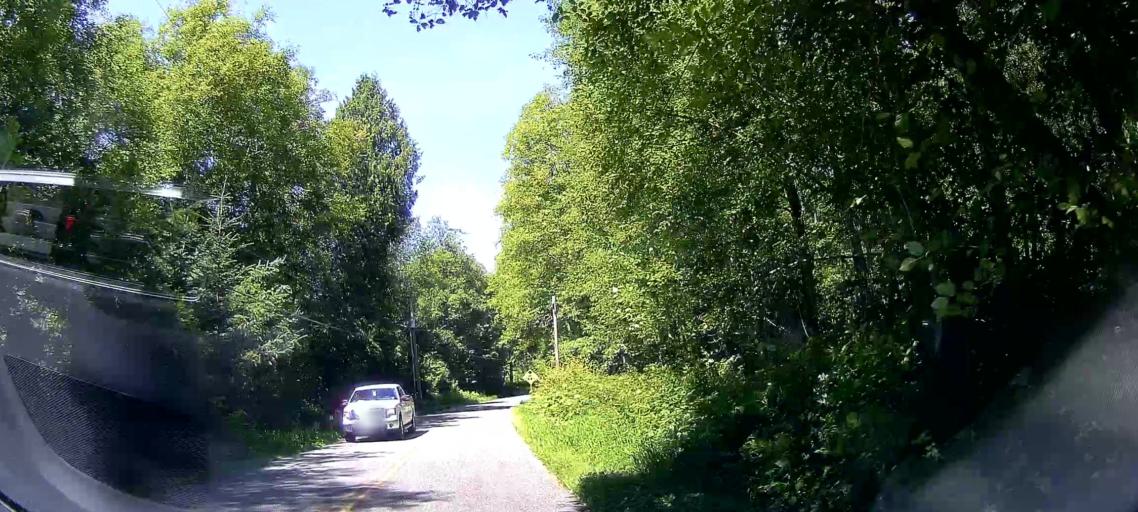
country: US
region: Washington
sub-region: Whatcom County
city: Sudden Valley
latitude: 48.6044
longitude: -122.3197
